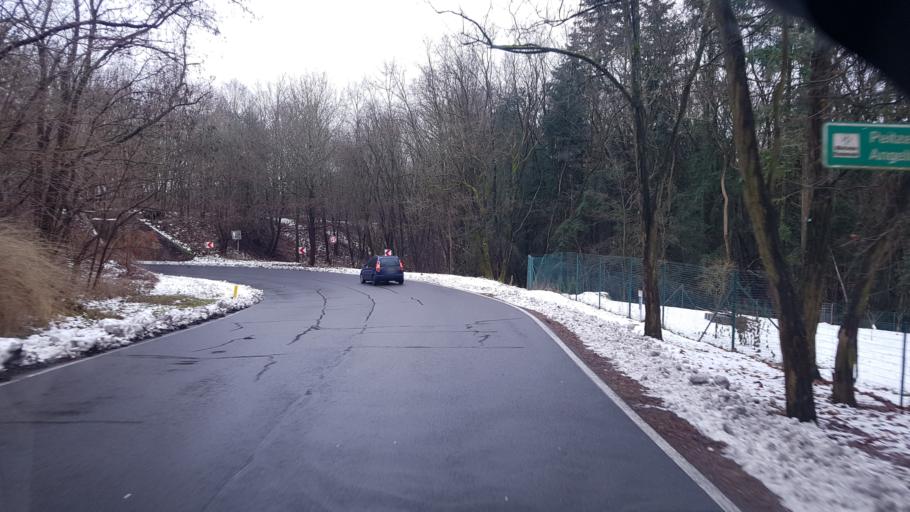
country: DE
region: Brandenburg
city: Jamlitz
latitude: 51.9894
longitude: 14.3712
